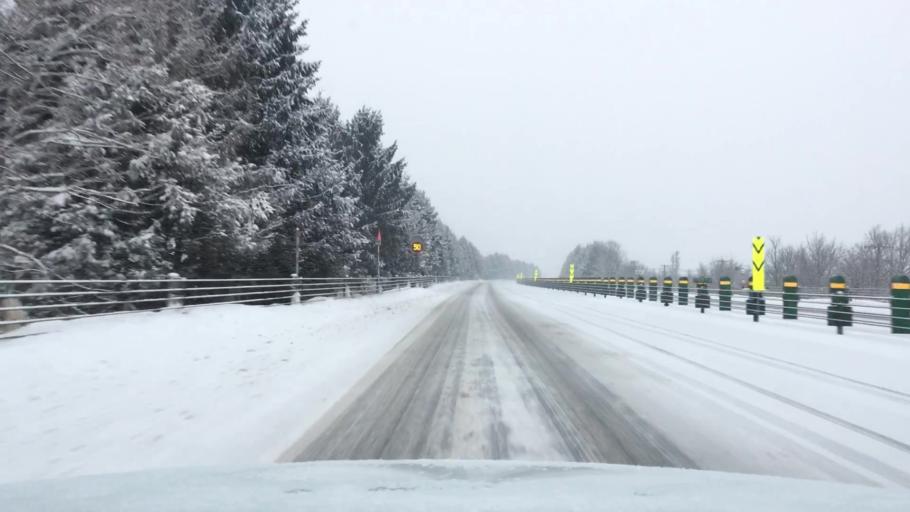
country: JP
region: Akita
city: Hanawa
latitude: 40.2677
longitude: 140.7647
